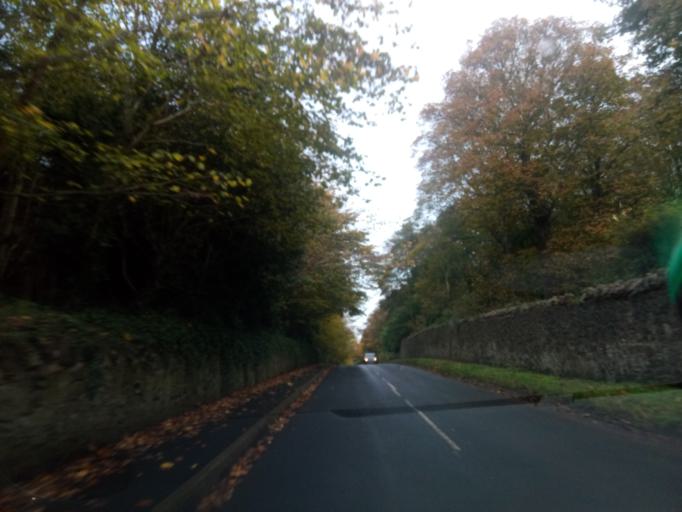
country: GB
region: Scotland
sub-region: The Scottish Borders
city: Eyemouth
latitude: 55.8445
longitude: -2.1199
